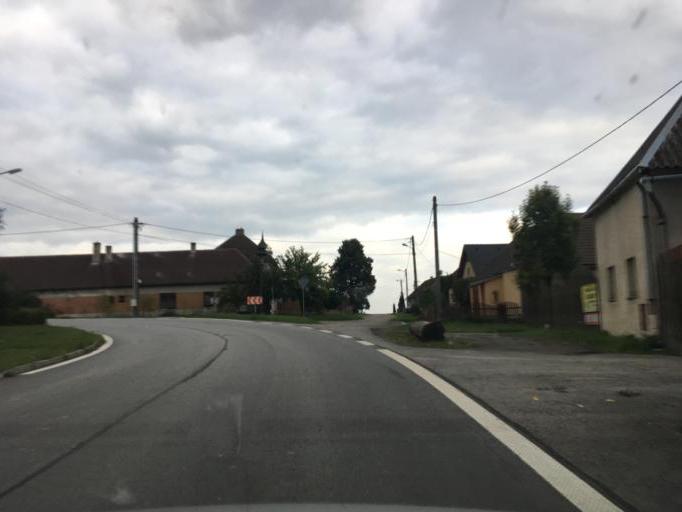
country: CZ
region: Vysocina
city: Zeletava
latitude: 49.1855
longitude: 15.6540
